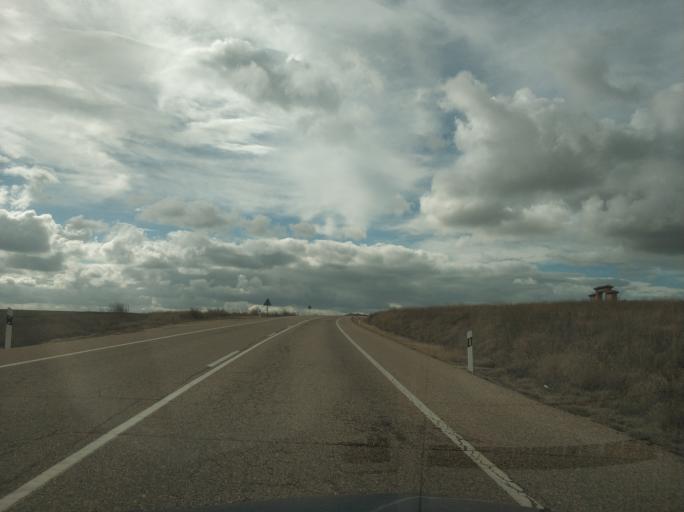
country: ES
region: Castille and Leon
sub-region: Provincia de Valladolid
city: Pollos
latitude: 41.4362
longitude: -5.0993
